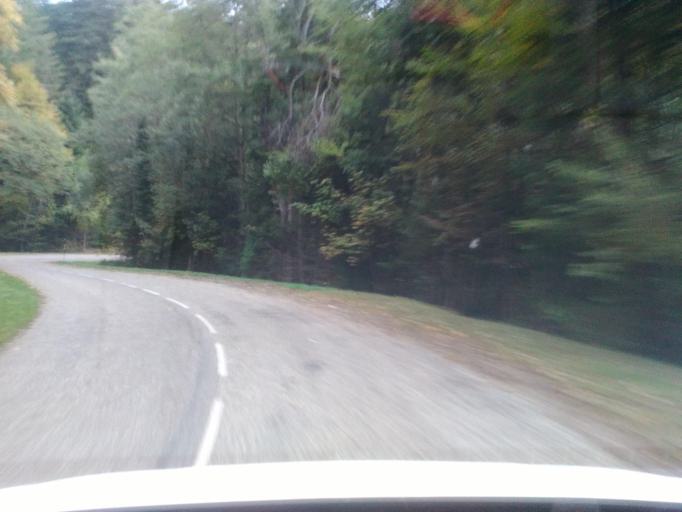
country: FR
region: Lorraine
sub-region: Departement des Vosges
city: Ban-de-Laveline
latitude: 48.3646
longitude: 7.1054
